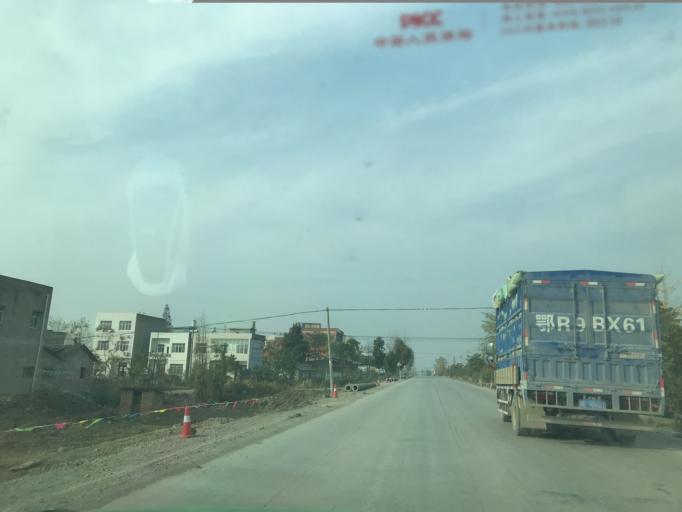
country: CN
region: Hubei
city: Tianmen
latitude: 30.7024
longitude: 113.1248
